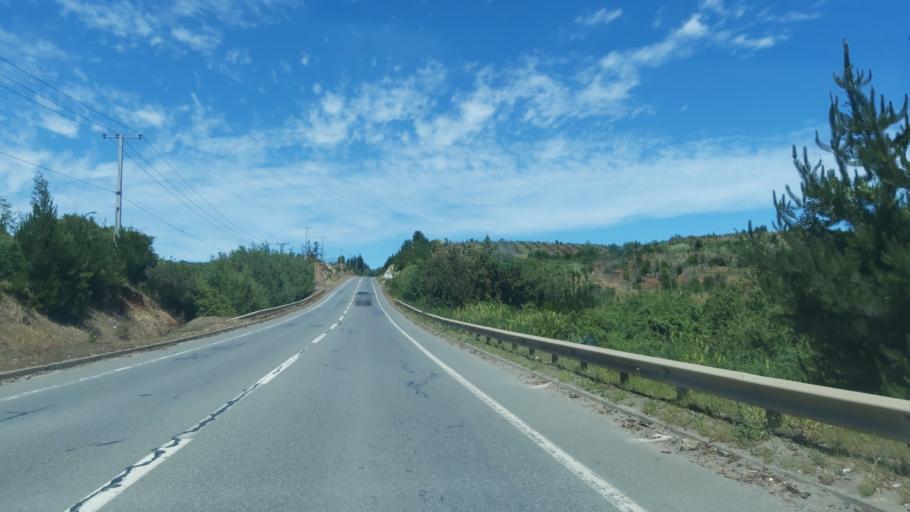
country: CL
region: Maule
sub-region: Provincia de Talca
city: Constitucion
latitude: -35.3197
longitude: -72.3854
